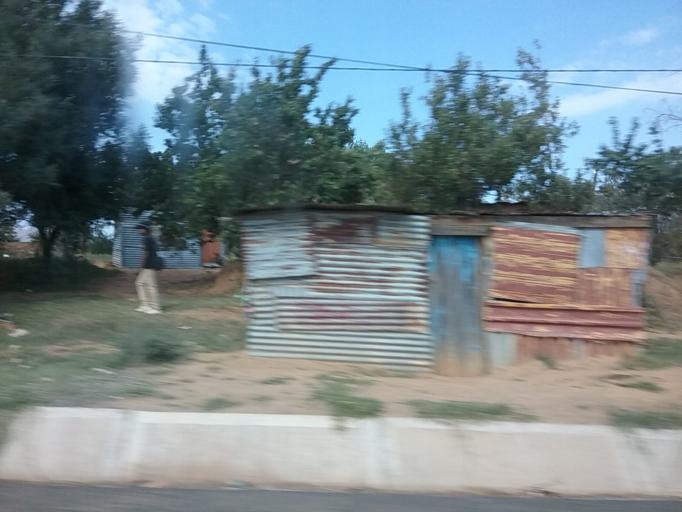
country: LS
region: Berea
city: Teyateyaneng
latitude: -29.1243
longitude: 27.9803
